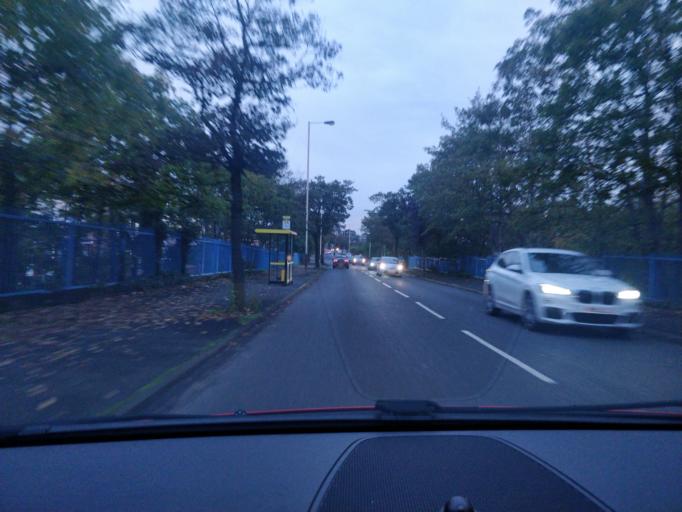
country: GB
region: England
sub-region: Sefton
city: Southport
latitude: 53.6458
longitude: -2.9761
